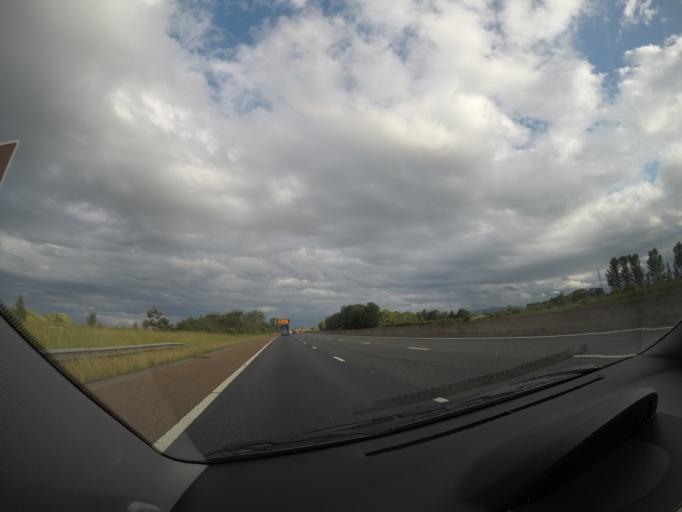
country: GB
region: England
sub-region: Cumbria
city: Penrith
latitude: 54.6724
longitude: -2.7764
